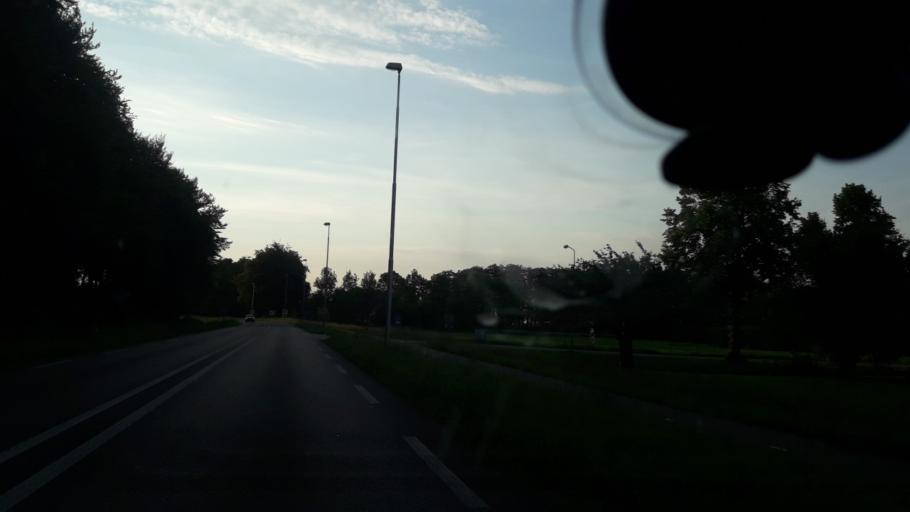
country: NL
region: Gelderland
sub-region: Gemeente Hattem
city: Hattem
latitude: 52.4714
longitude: 5.9824
